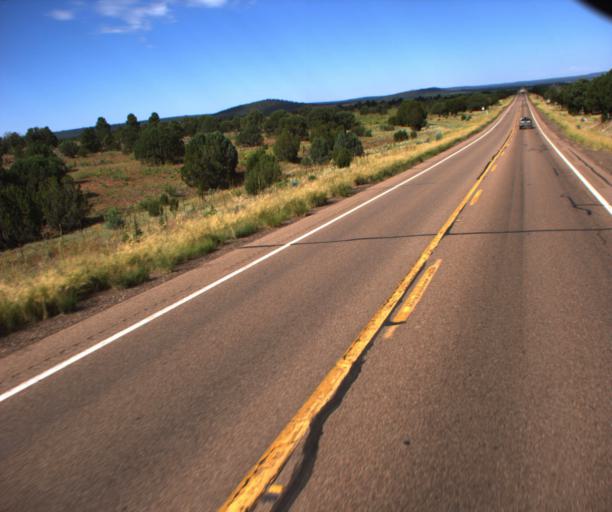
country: US
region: Arizona
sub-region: Navajo County
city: White Mountain Lake
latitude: 34.2747
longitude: -109.9015
